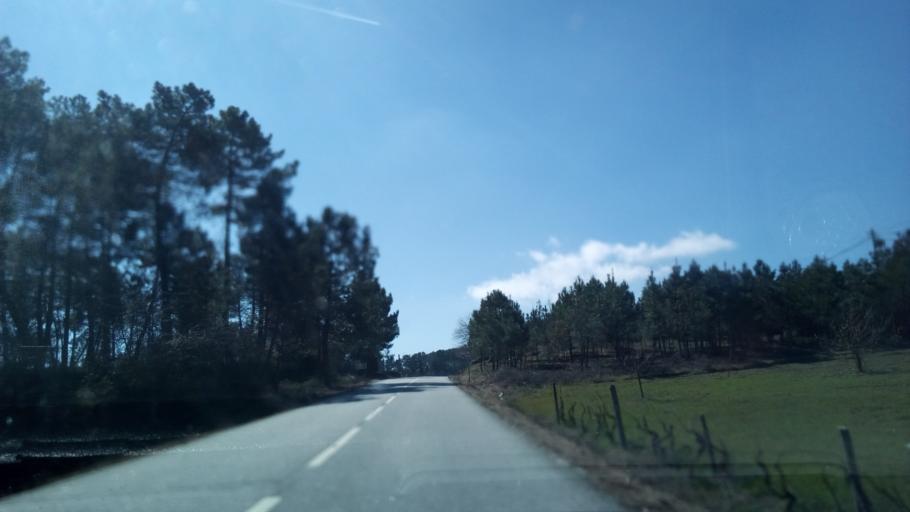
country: PT
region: Guarda
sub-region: Fornos de Algodres
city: Fornos de Algodres
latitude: 40.6451
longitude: -7.5317
